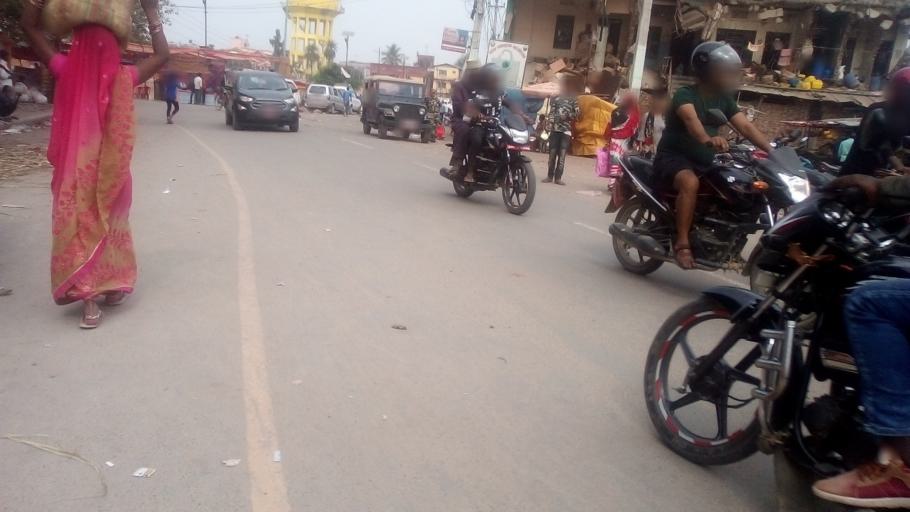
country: NP
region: Central Region
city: Janakpur
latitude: 26.7310
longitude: 85.9259
